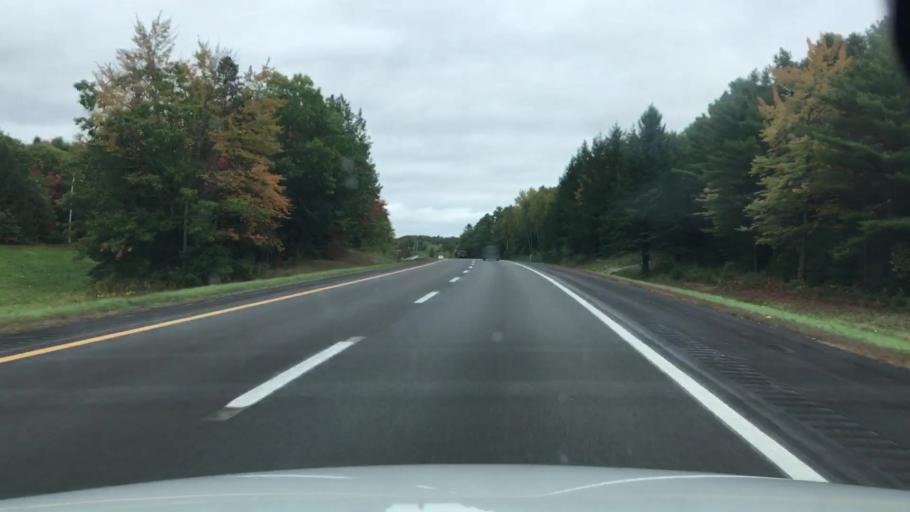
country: US
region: Maine
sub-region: Penobscot County
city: Veazie
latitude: 44.8651
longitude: -68.7090
